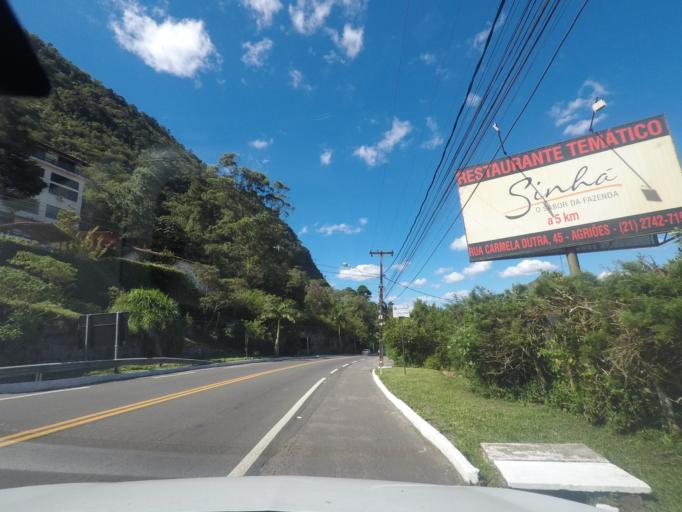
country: BR
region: Rio de Janeiro
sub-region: Teresopolis
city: Teresopolis
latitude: -22.4599
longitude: -42.9877
